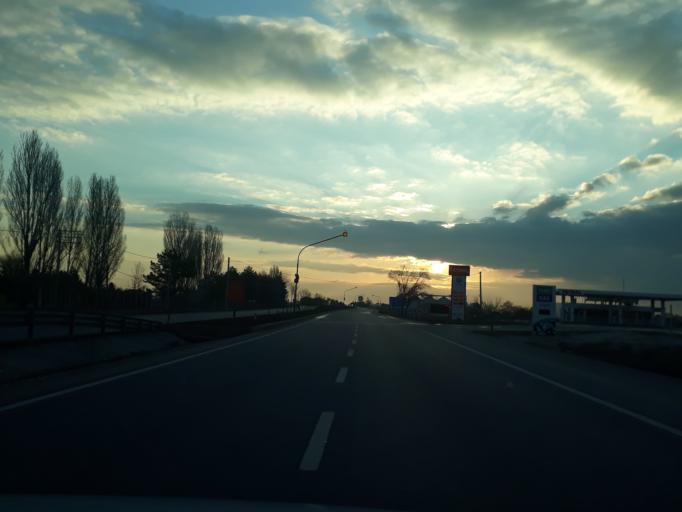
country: TR
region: Konya
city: Ovakavagi
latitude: 37.7385
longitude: 33.0406
